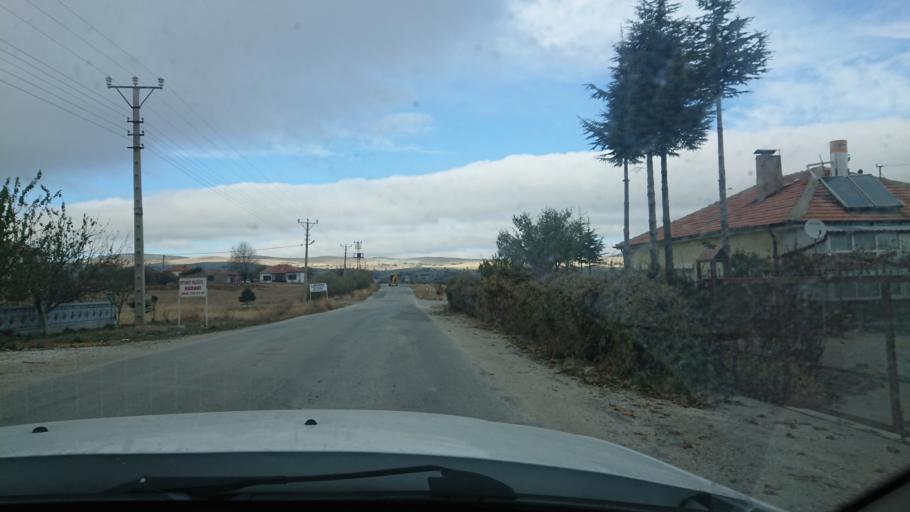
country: TR
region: Aksaray
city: Ortakoy
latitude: 38.7455
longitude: 34.0301
